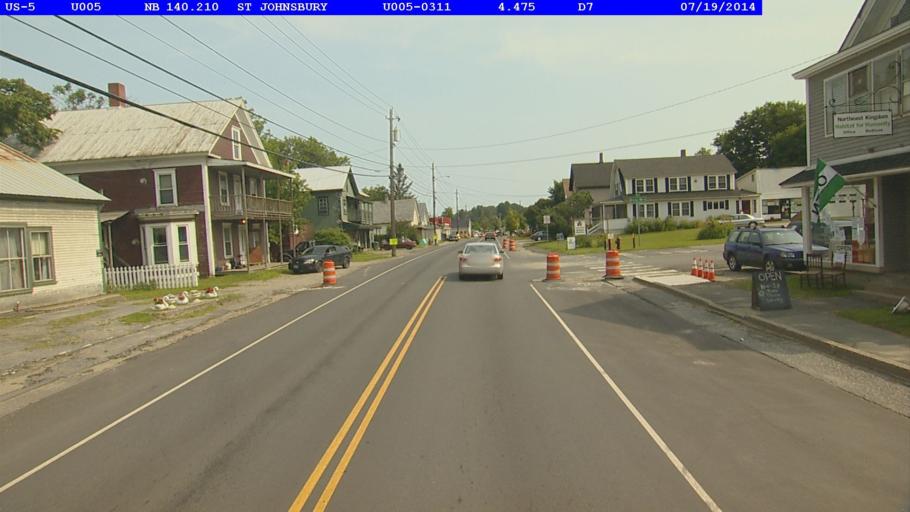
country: US
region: Vermont
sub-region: Caledonia County
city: St Johnsbury
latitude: 44.4557
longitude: -72.0162
